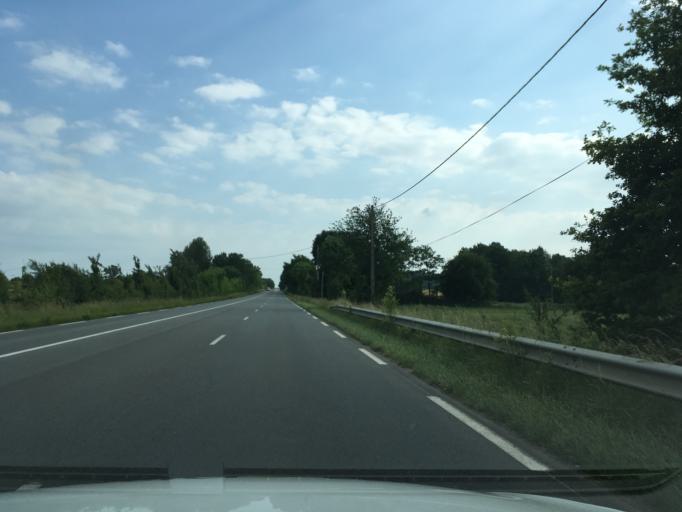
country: FR
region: Poitou-Charentes
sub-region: Departement des Deux-Sevres
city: Le Tallud
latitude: 46.6092
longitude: -0.2856
